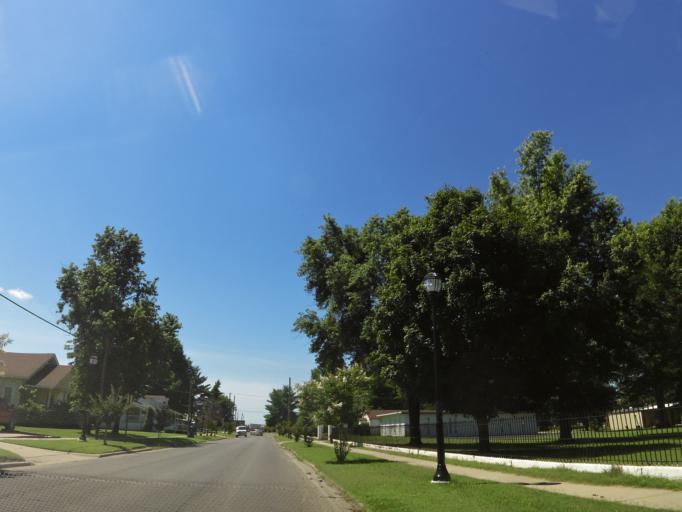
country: US
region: Missouri
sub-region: New Madrid County
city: New Madrid
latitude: 36.5912
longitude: -89.5271
